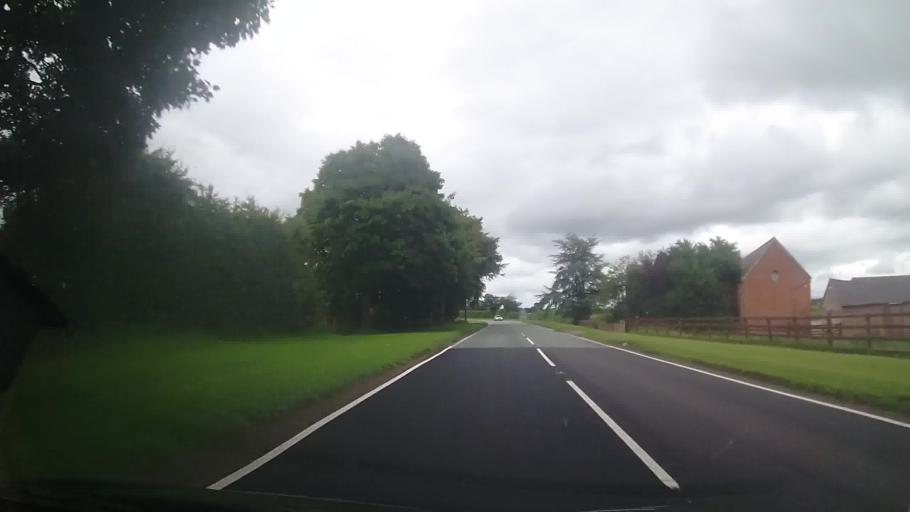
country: GB
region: England
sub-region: Shropshire
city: Ellesmere
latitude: 52.9332
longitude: -2.7976
